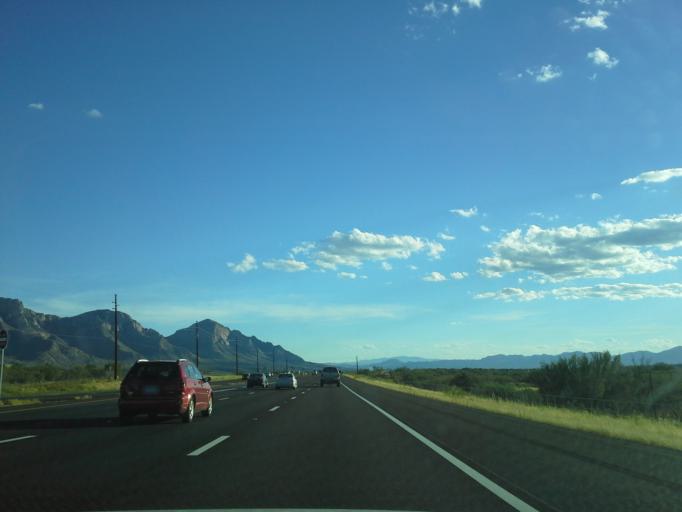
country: US
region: Arizona
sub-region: Pima County
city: Catalina
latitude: 32.4656
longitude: -110.9264
